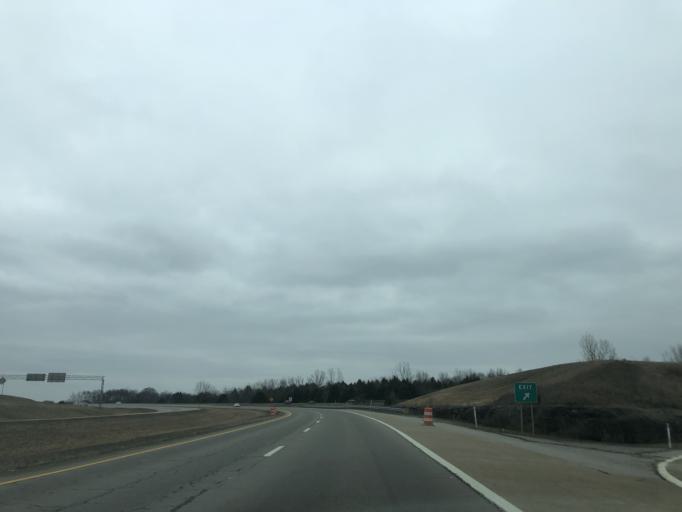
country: US
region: Tennessee
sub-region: Maury County
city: Spring Hill
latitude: 35.7372
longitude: -86.9465
